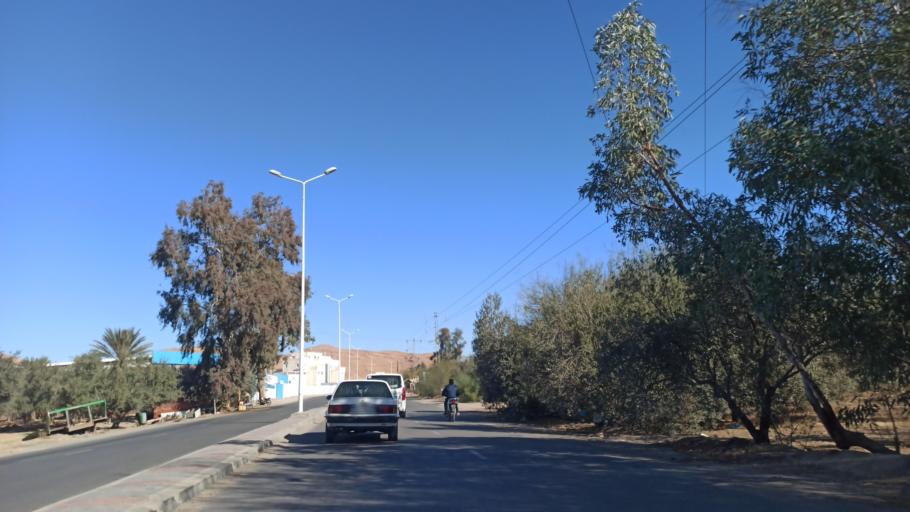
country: TN
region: Gafsa
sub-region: Gafsa Municipality
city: Gafsa
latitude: 34.4198
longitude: 8.7451
